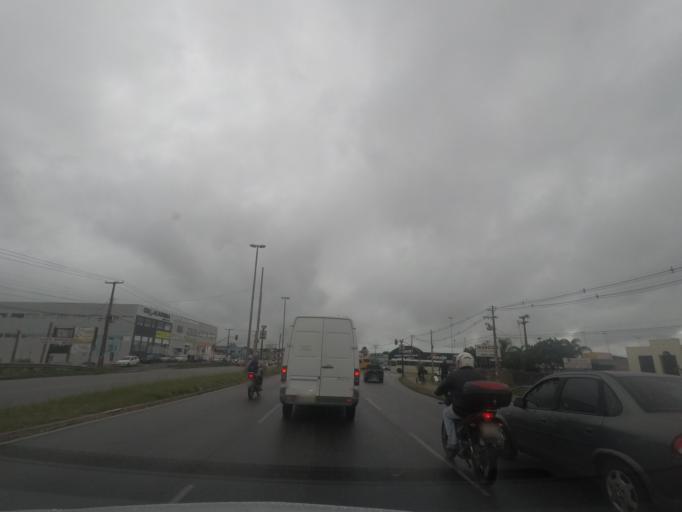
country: BR
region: Parana
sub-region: Colombo
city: Colombo
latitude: -25.3488
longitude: -49.1705
